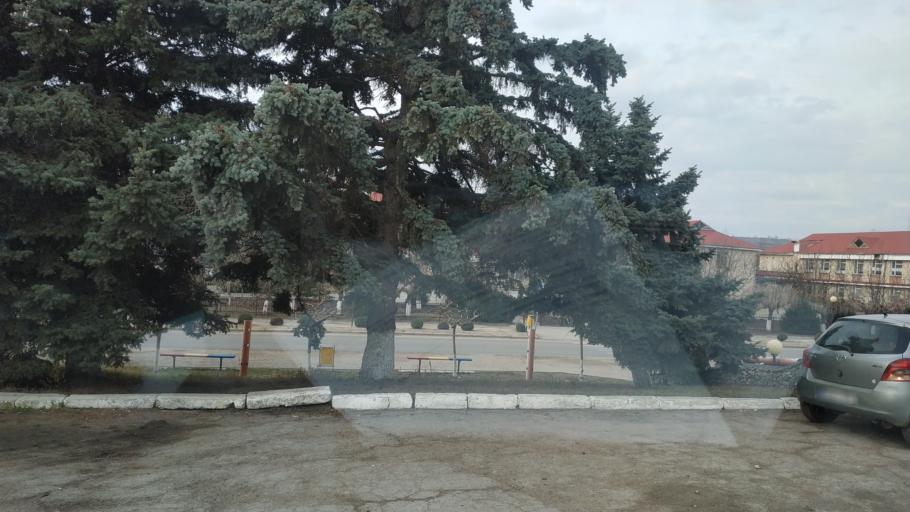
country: MD
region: Chisinau
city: Singera
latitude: 46.9630
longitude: 29.0568
